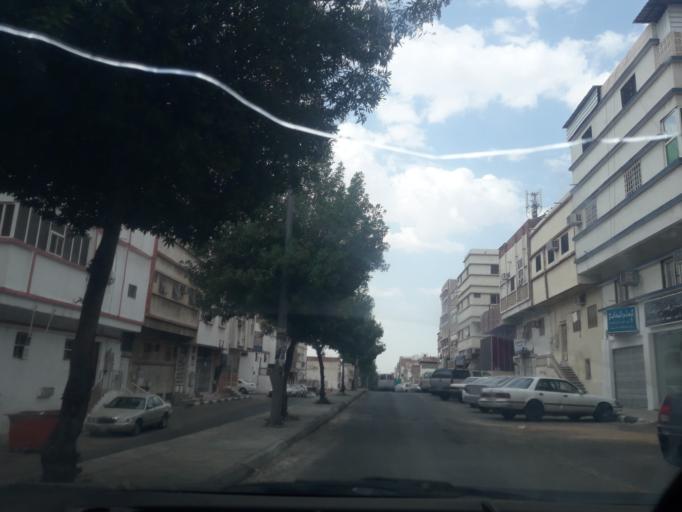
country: SA
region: Makkah
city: Ta'if
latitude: 21.2609
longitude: 40.4197
